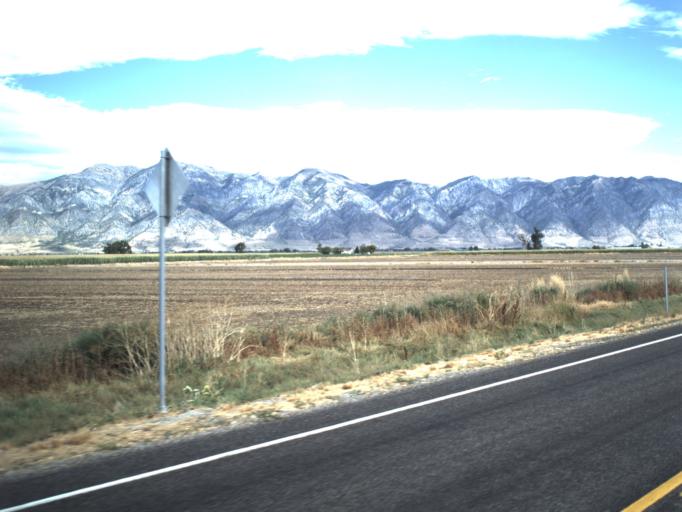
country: US
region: Utah
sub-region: Box Elder County
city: Honeyville
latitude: 41.5629
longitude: -112.1668
